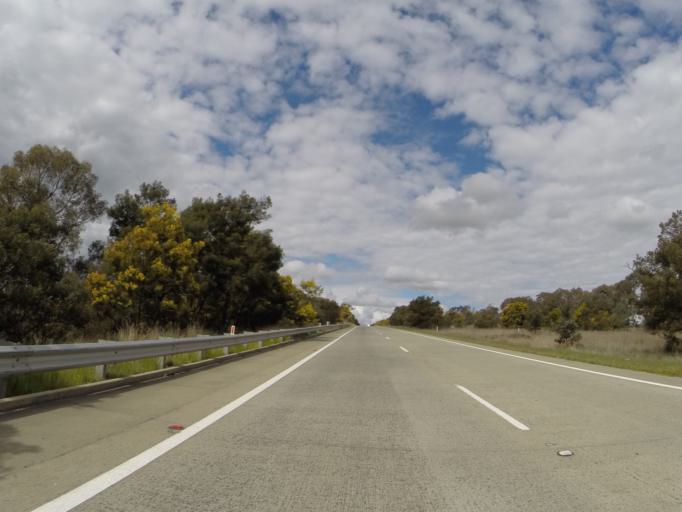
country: AU
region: New South Wales
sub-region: Yass Valley
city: Gundaroo
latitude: -34.8196
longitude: 149.3473
